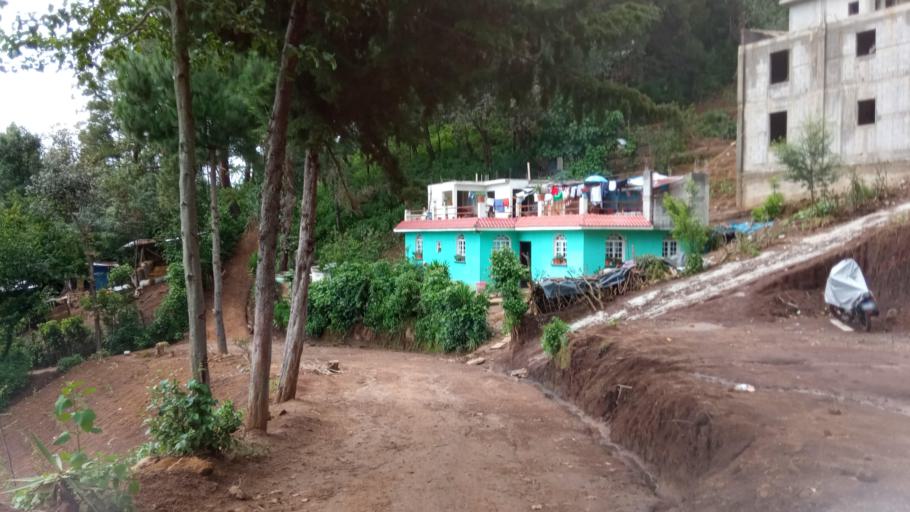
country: GT
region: San Marcos
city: Tejutla
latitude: 15.1171
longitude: -91.8036
